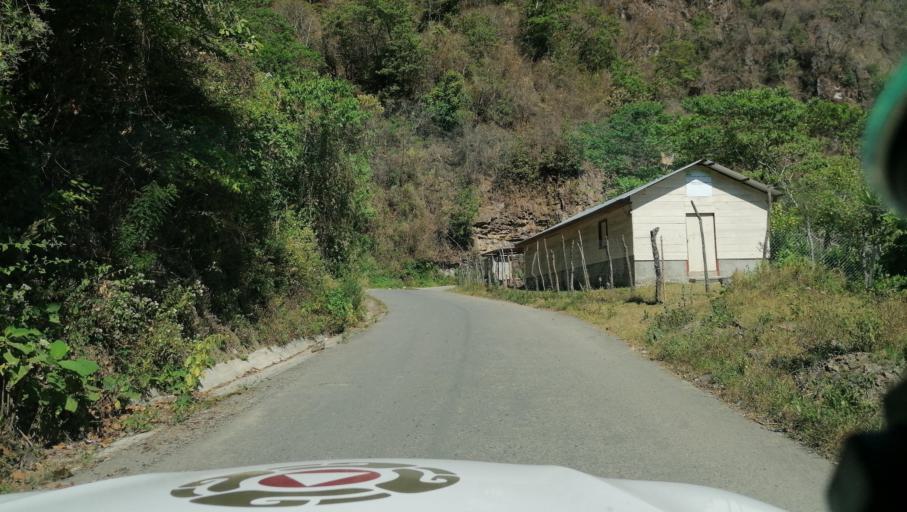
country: MX
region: Chiapas
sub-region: Cacahoatan
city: Benito Juarez
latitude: 15.1822
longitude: -92.1916
